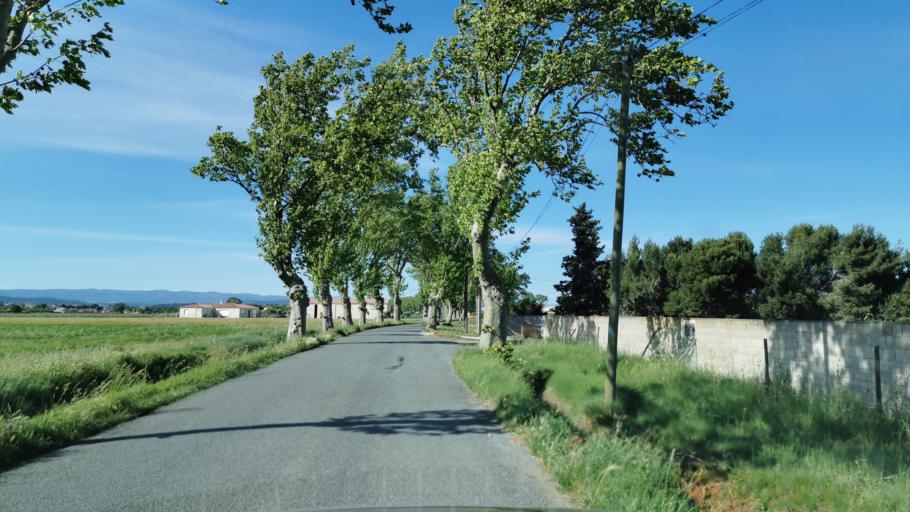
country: FR
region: Languedoc-Roussillon
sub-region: Departement de l'Aude
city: Canet
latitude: 43.2144
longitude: 2.8444
